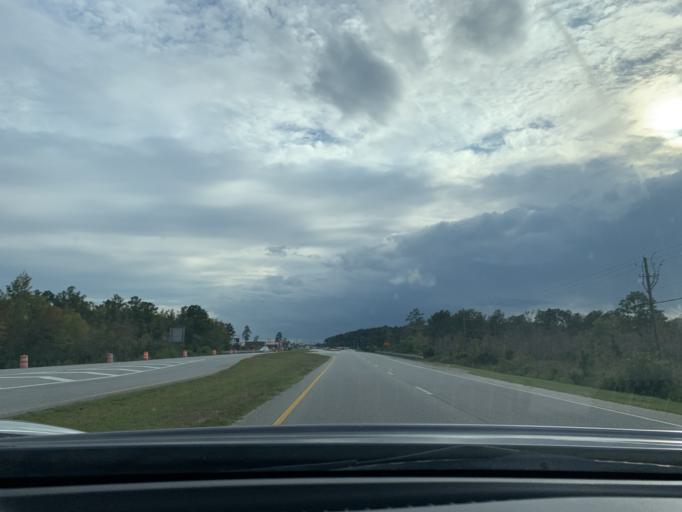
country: US
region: Georgia
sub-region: Chatham County
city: Pooler
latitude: 32.1015
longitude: -81.2694
